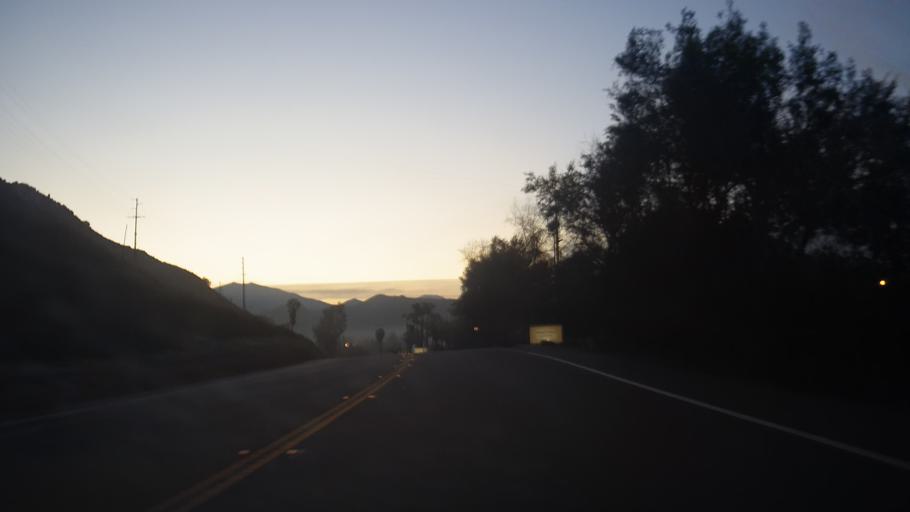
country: US
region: California
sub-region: San Diego County
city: Granite Hills
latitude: 32.7876
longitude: -116.8861
